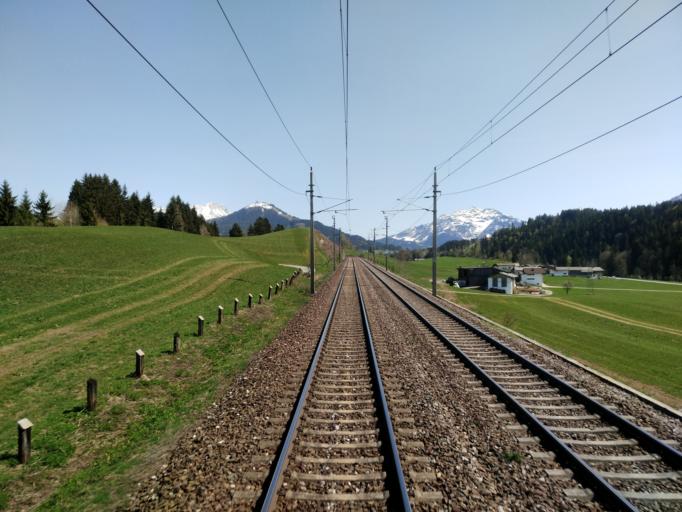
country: AT
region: Tyrol
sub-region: Politischer Bezirk Kitzbuhel
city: Fieberbrunn
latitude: 47.4975
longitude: 12.4988
